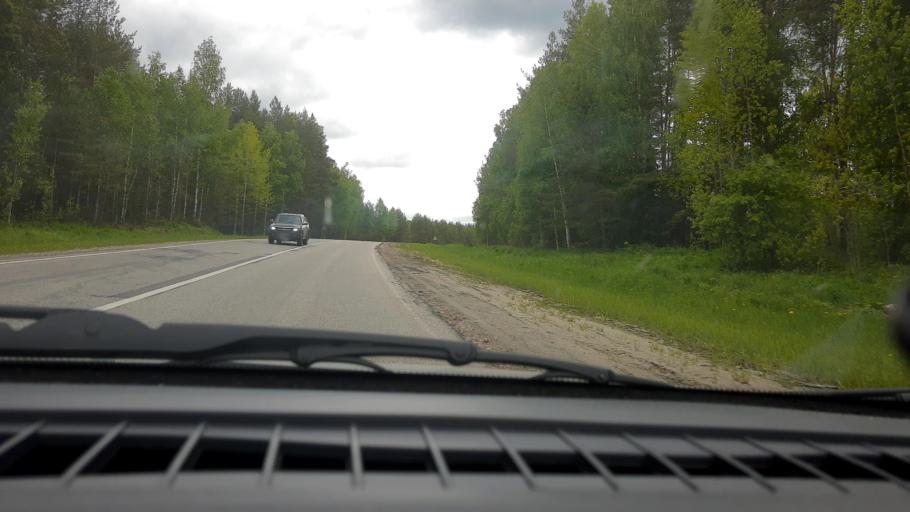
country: RU
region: Nizjnij Novgorod
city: Krasnyye Baki
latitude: 56.9879
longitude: 45.1175
